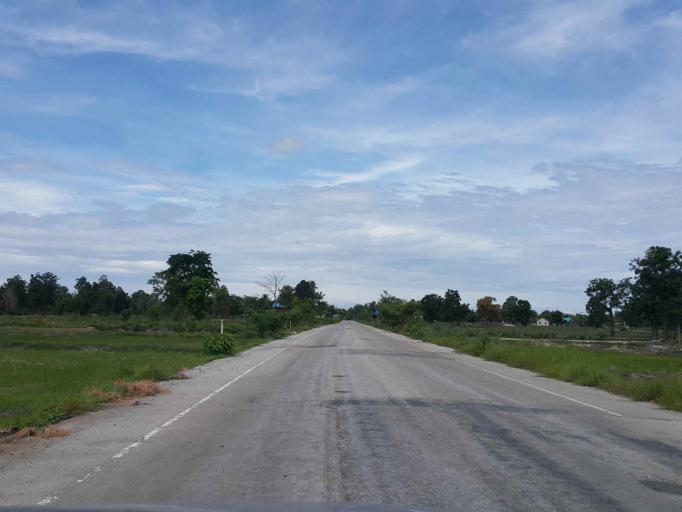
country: TH
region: Sukhothai
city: Ban Dan Lan Hoi
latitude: 17.1092
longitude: 99.4854
